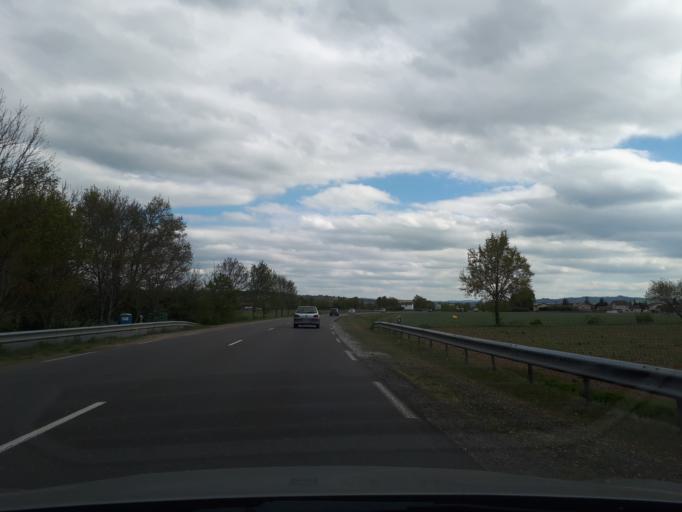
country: FR
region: Rhone-Alpes
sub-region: Departement de la Loire
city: Chamboeuf
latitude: 45.5669
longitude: 4.3099
